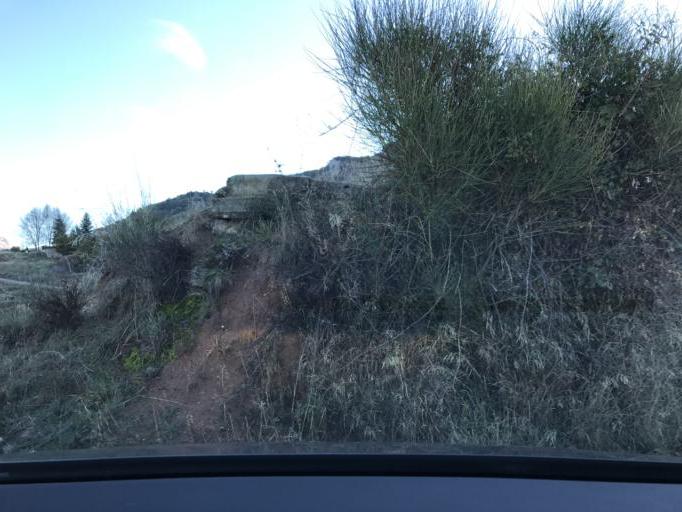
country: ES
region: Andalusia
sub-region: Provincia de Granada
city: Nivar
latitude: 37.2660
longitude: -3.5716
